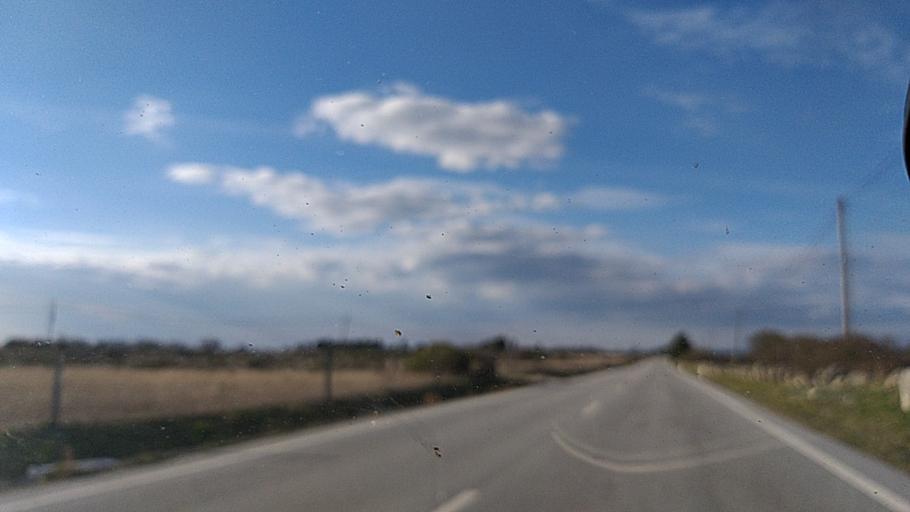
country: ES
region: Castille and Leon
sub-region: Provincia de Salamanca
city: Fuentes de Onoro
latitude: 40.6272
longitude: -6.8500
